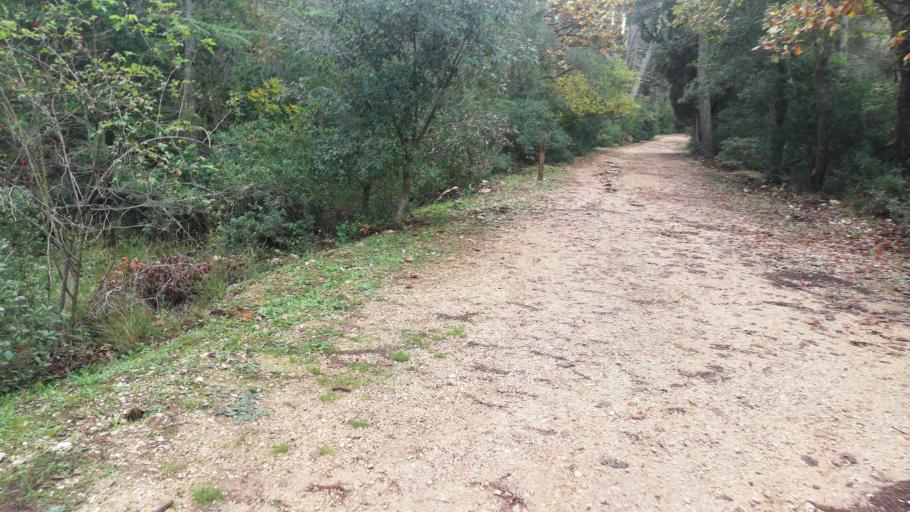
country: IT
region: Apulia
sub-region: Provincia di Bari
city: Cassano delle Murge
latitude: 40.8799
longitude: 16.7117
